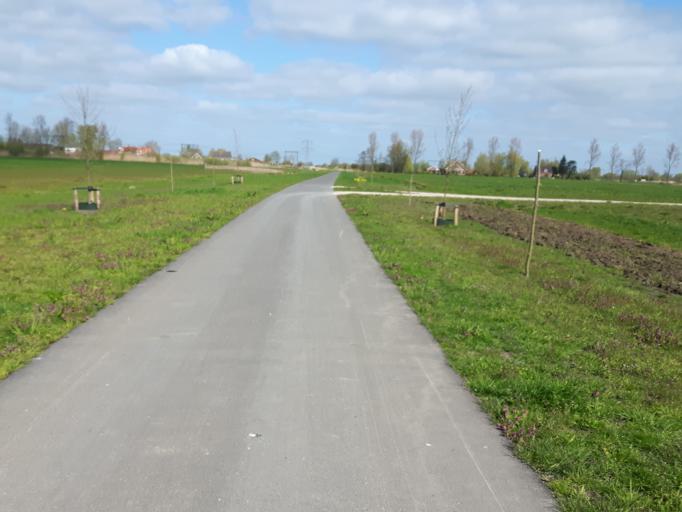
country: NL
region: Utrecht
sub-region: Stichtse Vecht
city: Spechtenkamp
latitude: 52.1264
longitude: 4.9763
